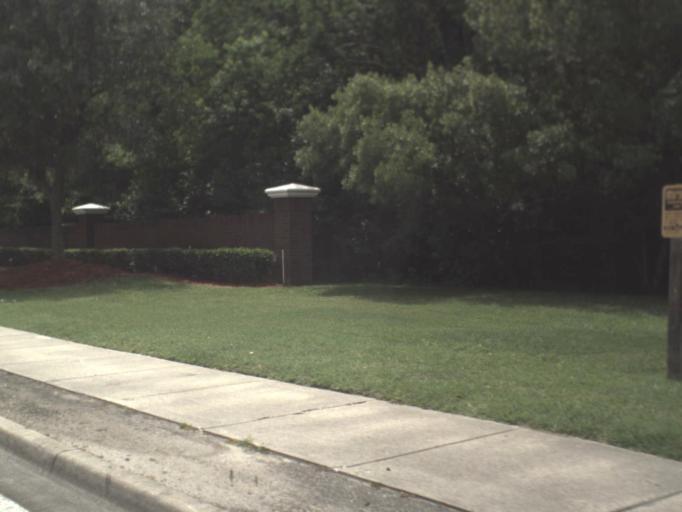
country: US
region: Florida
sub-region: Duval County
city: Jacksonville
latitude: 30.4385
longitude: -81.7056
